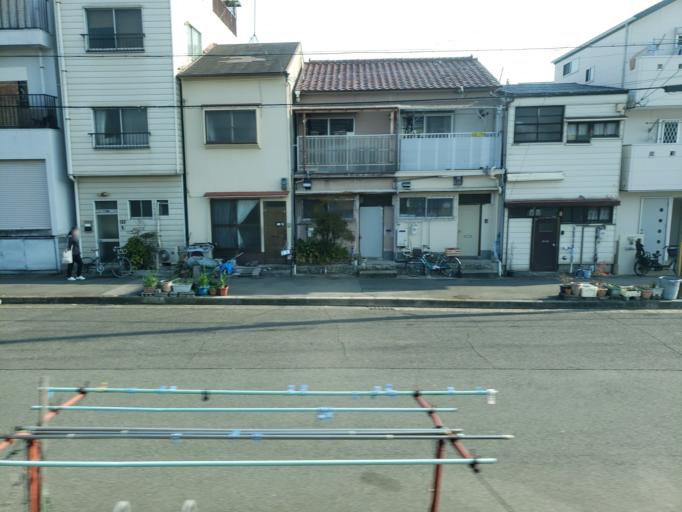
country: JP
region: Hyogo
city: Kobe
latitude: 34.7110
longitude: 135.2316
